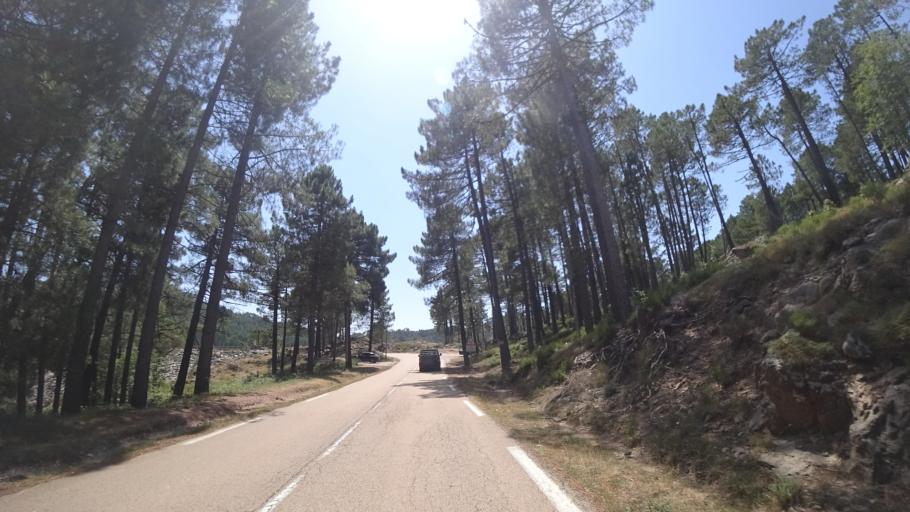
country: FR
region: Corsica
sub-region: Departement de la Corse-du-Sud
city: Zonza
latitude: 41.6700
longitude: 9.2066
